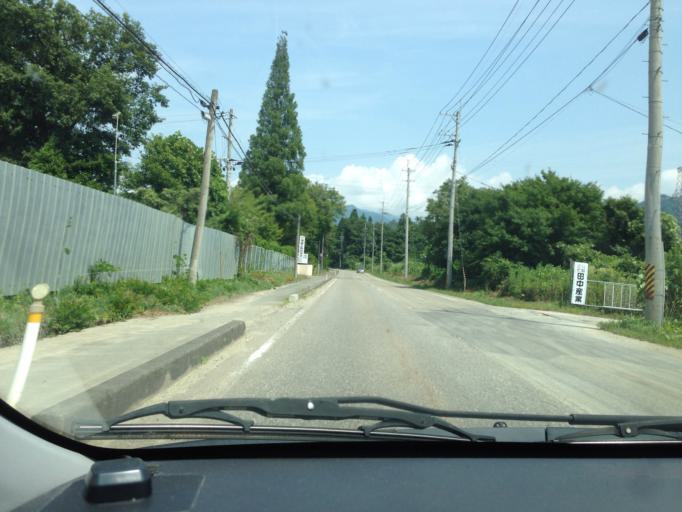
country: JP
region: Fukushima
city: Kitakata
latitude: 37.7052
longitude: 139.8774
